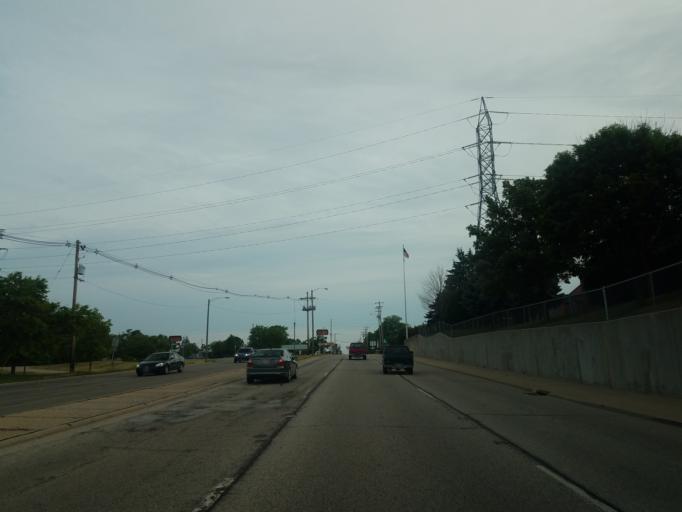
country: US
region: Illinois
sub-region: McLean County
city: Bloomington
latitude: 40.4606
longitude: -88.9929
